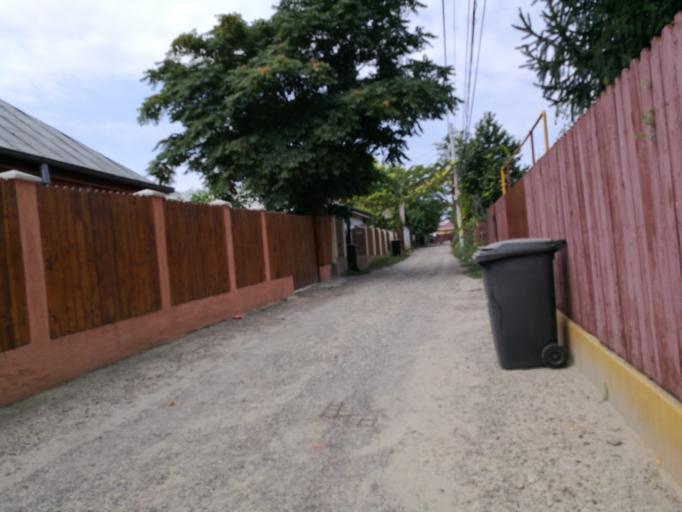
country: RO
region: Iasi
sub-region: Comuna Miroslava
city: Miroslava
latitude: 47.1745
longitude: 27.5317
